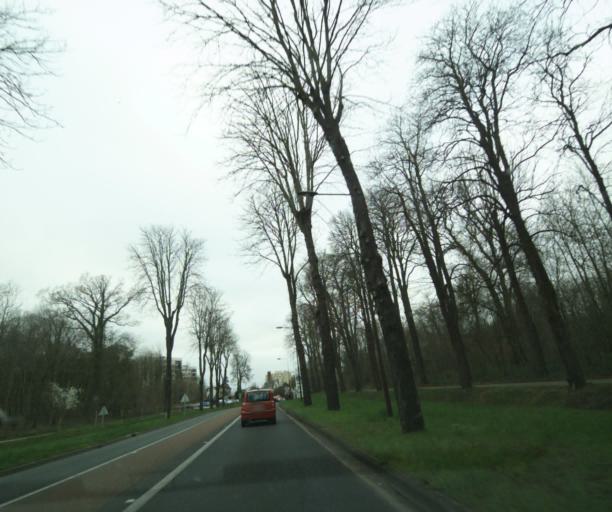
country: FR
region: Ile-de-France
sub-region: Departement des Yvelines
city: Poissy
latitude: 48.9228
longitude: 2.0554
